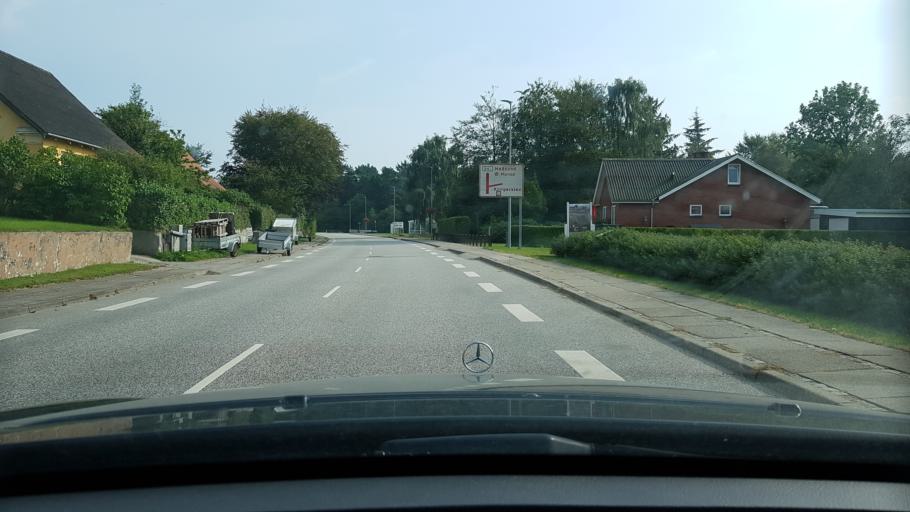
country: DK
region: North Denmark
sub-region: Alborg Kommune
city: Hals
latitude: 56.9029
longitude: 10.2545
